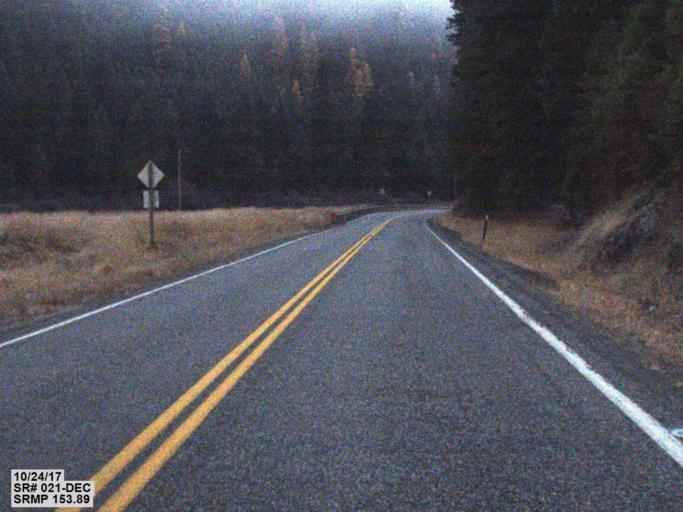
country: US
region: Washington
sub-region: Ferry County
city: Republic
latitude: 48.5557
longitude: -118.7442
